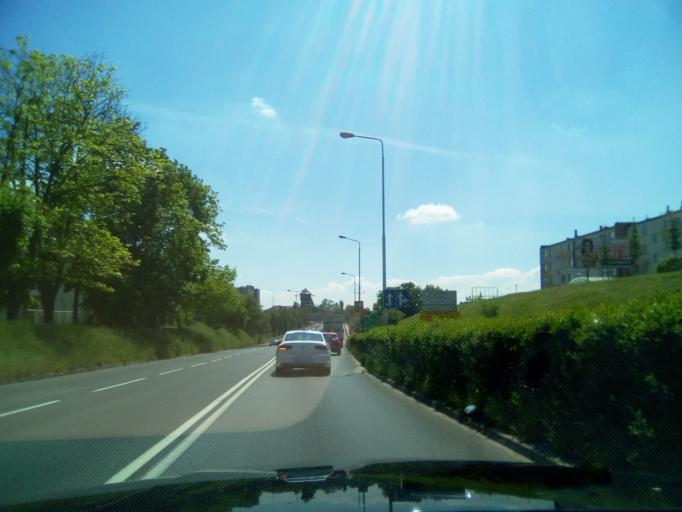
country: PL
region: Greater Poland Voivodeship
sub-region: Powiat gnieznienski
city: Gniezno
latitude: 52.5474
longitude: 17.6037
